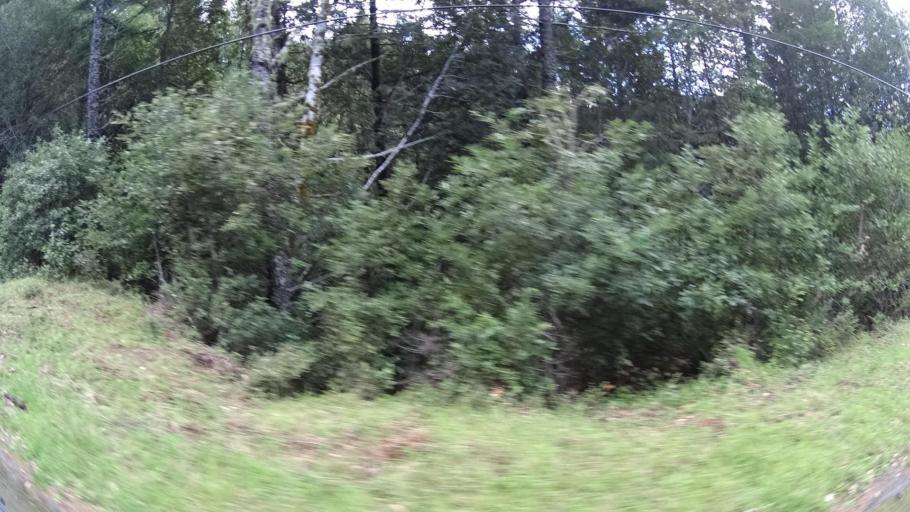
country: US
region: California
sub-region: Humboldt County
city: Bayside
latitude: 40.7520
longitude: -123.9719
